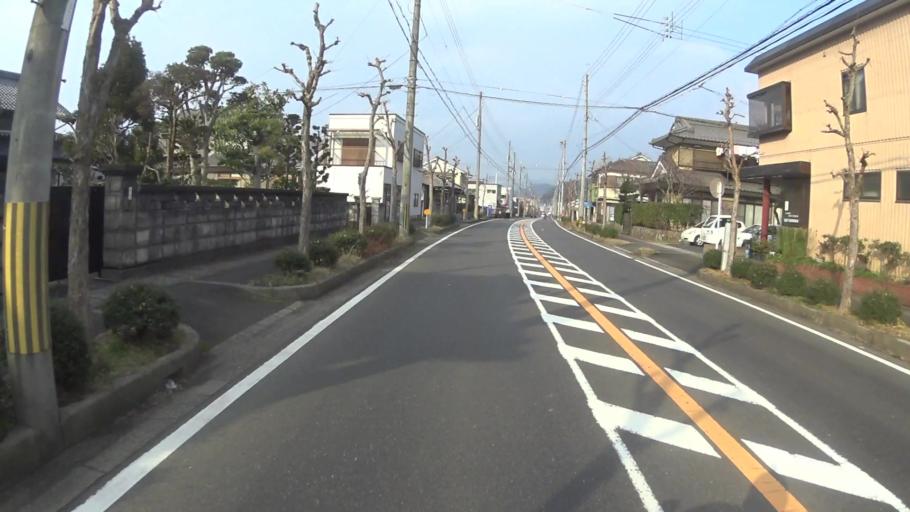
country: JP
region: Kyoto
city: Maizuru
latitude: 35.4522
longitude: 135.3991
